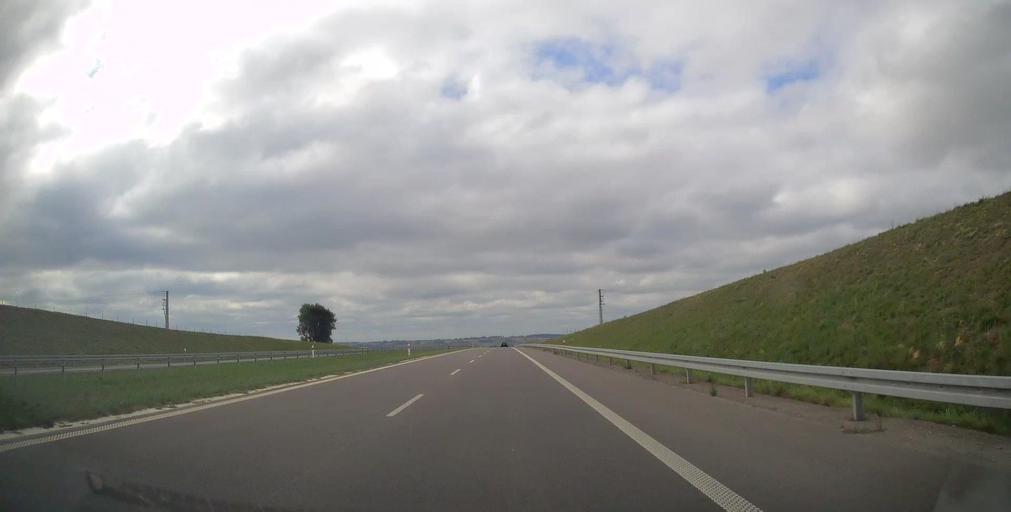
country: PL
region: Lesser Poland Voivodeship
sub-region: Powiat krakowski
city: Slomniki
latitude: 50.2532
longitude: 20.0169
